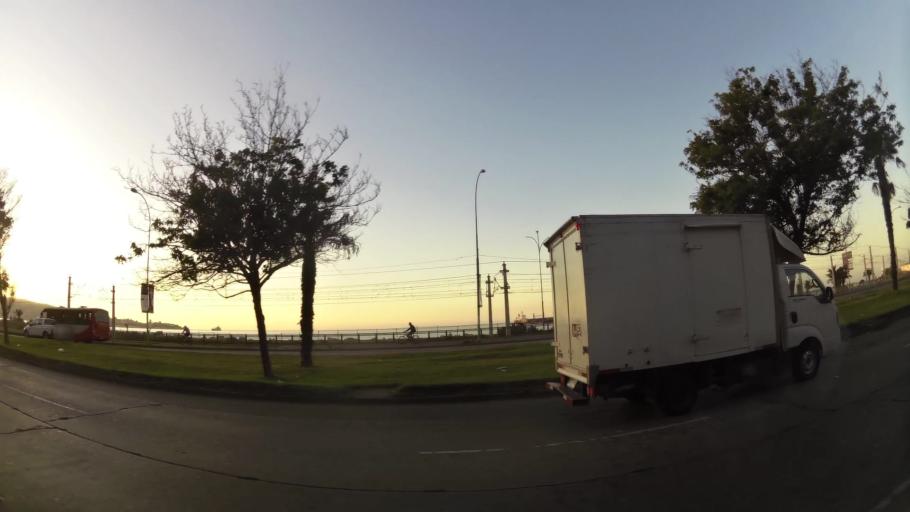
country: CL
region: Valparaiso
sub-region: Provincia de Valparaiso
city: Vina del Mar
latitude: -33.0302
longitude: -71.5873
